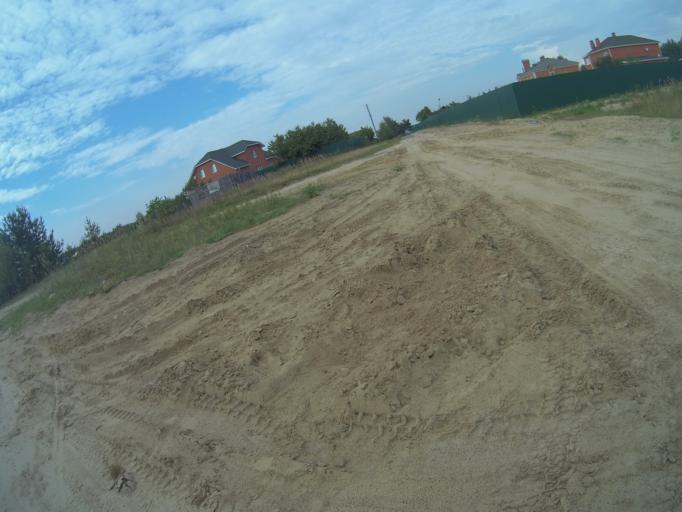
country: RU
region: Vladimir
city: Raduzhnyy
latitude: 56.0044
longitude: 40.3128
